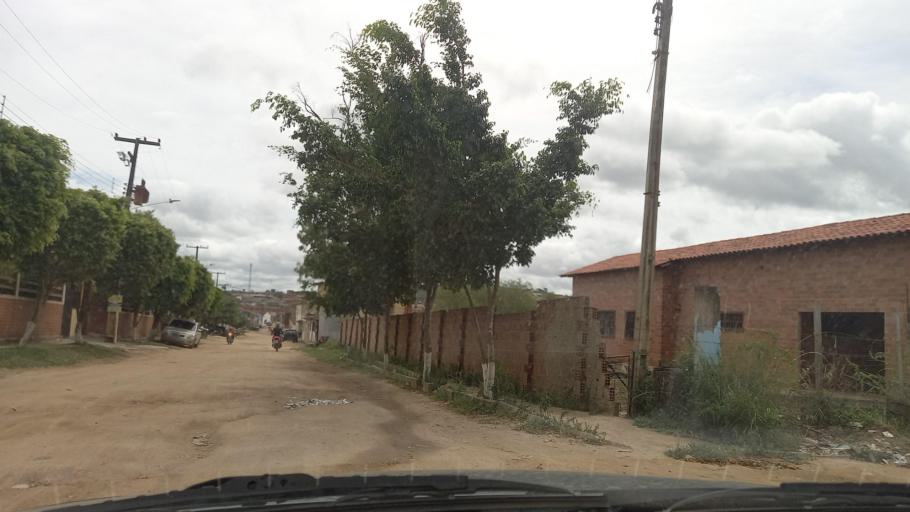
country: ET
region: Oromiya
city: Gore
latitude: 8.1965
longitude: 35.5797
